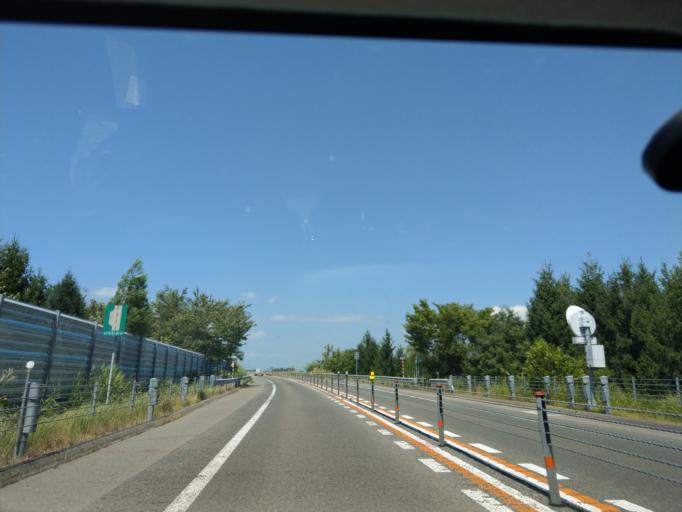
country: JP
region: Akita
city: Yokotemachi
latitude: 39.3514
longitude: 140.4969
